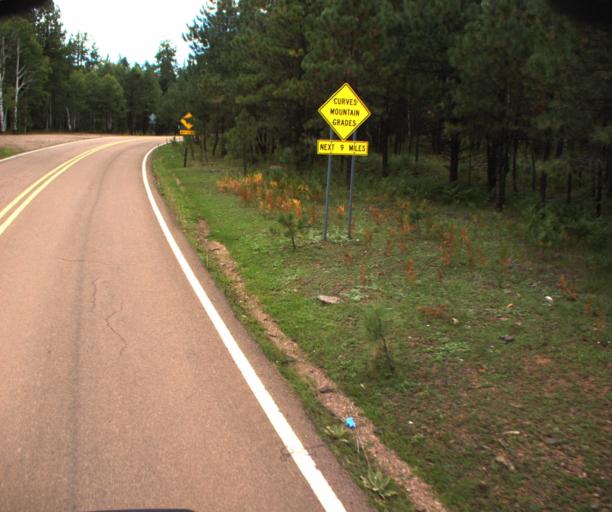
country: US
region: Arizona
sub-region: Navajo County
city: Pinetop-Lakeside
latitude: 33.9984
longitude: -109.7511
